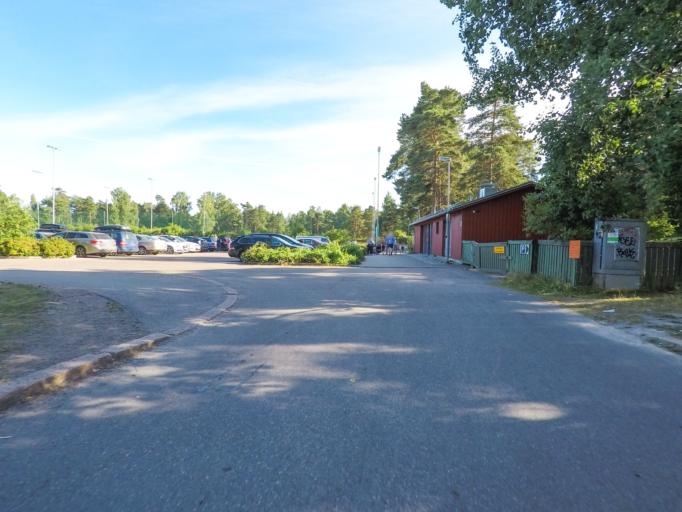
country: FI
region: Uusimaa
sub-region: Helsinki
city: Helsinki
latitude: 60.1819
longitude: 24.9901
